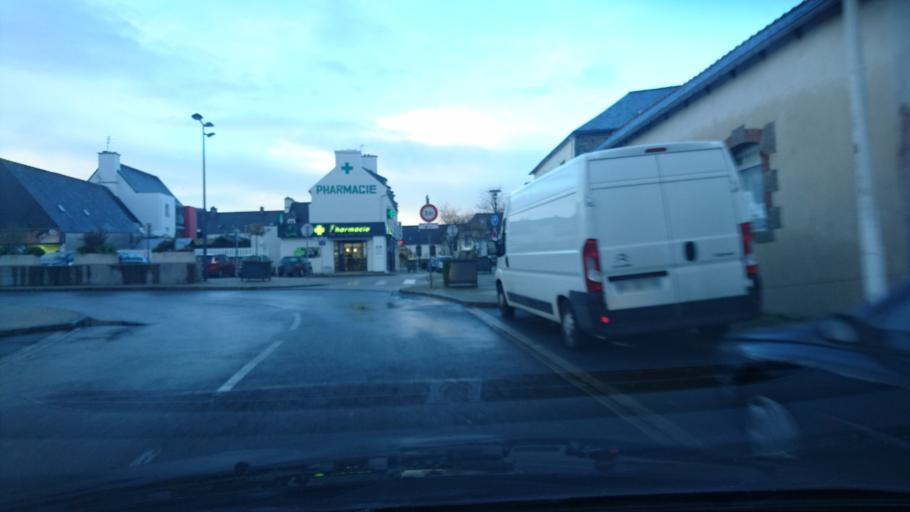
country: FR
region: Brittany
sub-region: Departement du Finistere
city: Guilers
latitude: 48.4241
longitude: -4.5588
